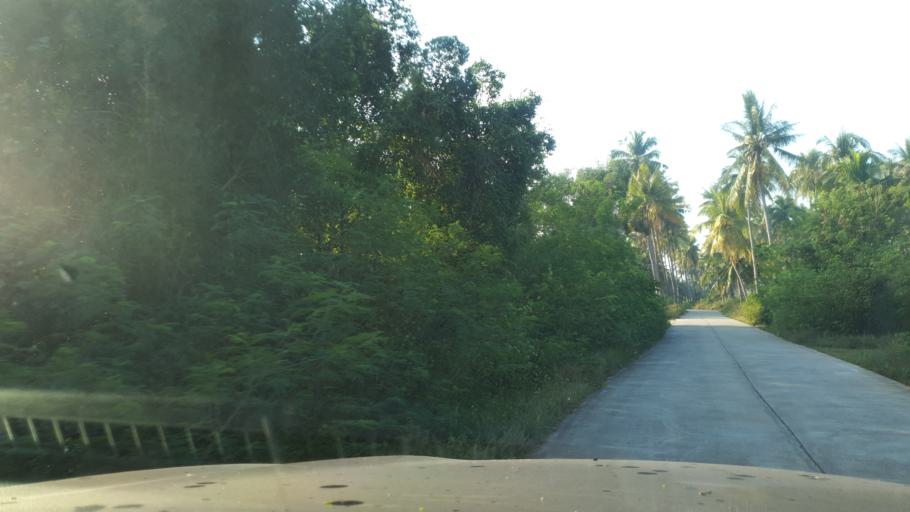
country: TH
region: Prachuap Khiri Khan
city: Bang Saphan
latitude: 11.3009
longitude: 99.5499
